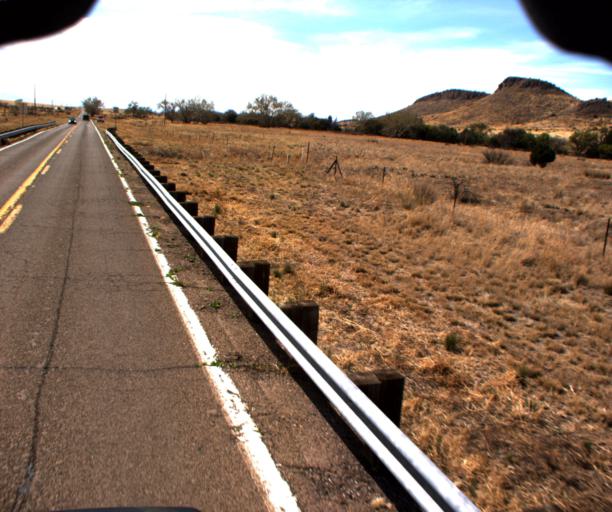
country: US
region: Arizona
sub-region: Cochise County
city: Willcox
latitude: 32.0066
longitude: -109.3913
